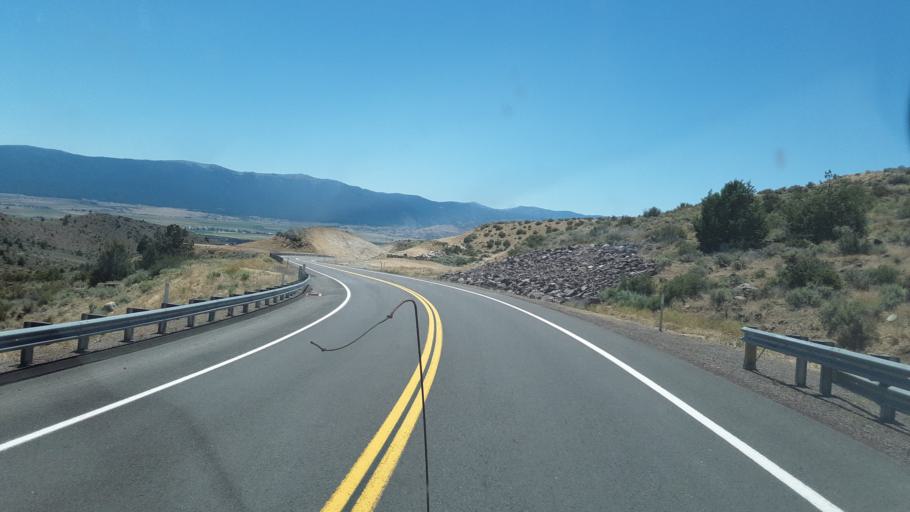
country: US
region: California
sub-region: Lassen County
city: Johnstonville
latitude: 40.4630
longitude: -120.5768
